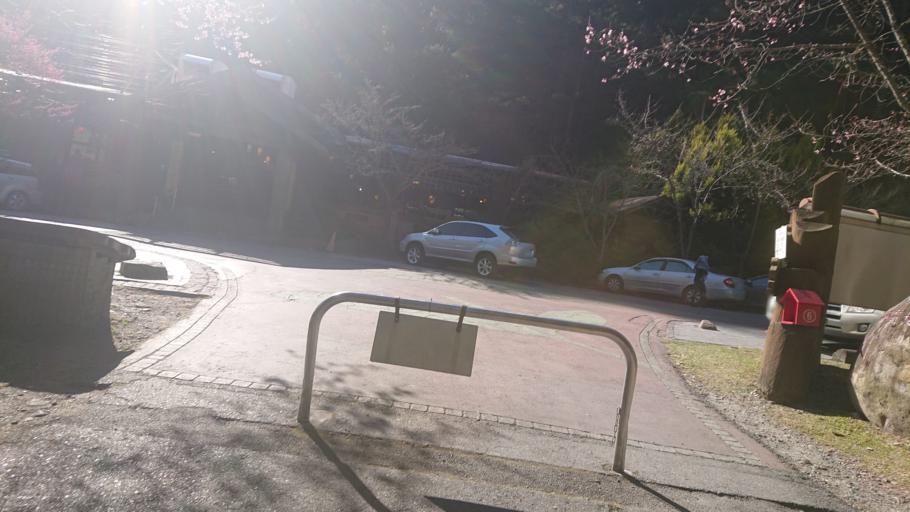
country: TW
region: Taiwan
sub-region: Hualien
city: Hualian
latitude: 24.3574
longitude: 121.3124
